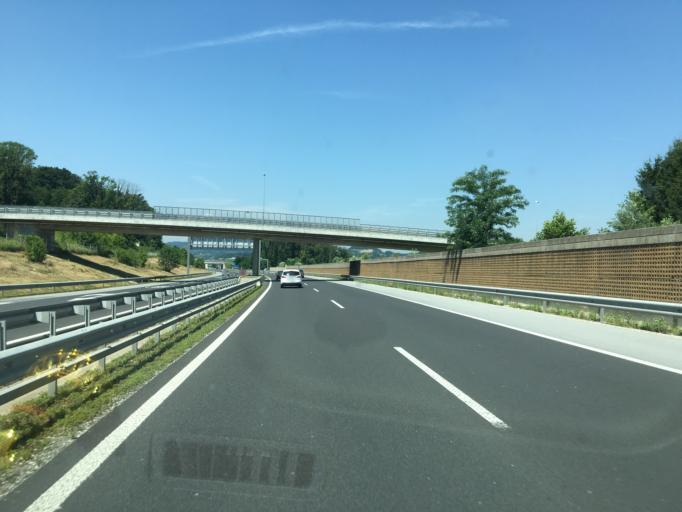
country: SI
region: Pesnica
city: Pesnica pri Mariboru
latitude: 46.5914
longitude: 15.6821
